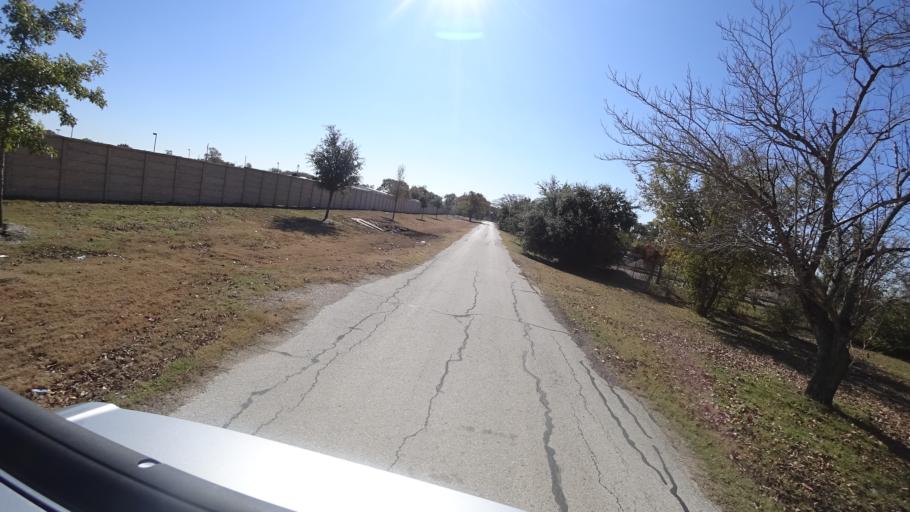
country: US
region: Texas
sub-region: Denton County
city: Lewisville
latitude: 33.0436
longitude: -96.9405
